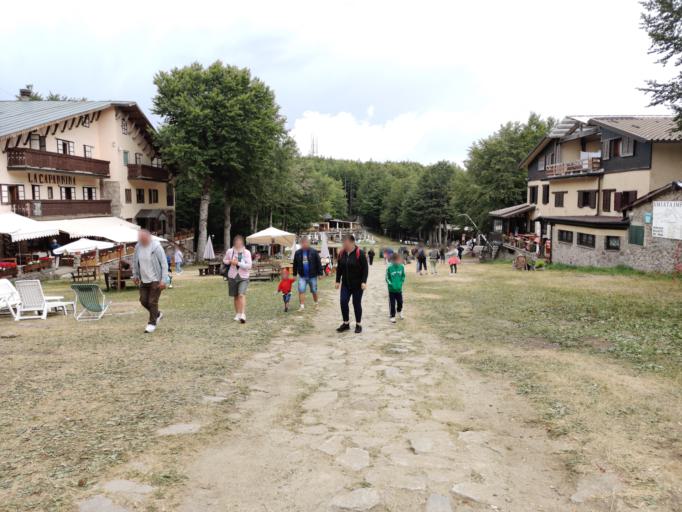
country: IT
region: Tuscany
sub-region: Provincia di Siena
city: Abbadia San Salvatore
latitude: 42.8903
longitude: 11.6260
